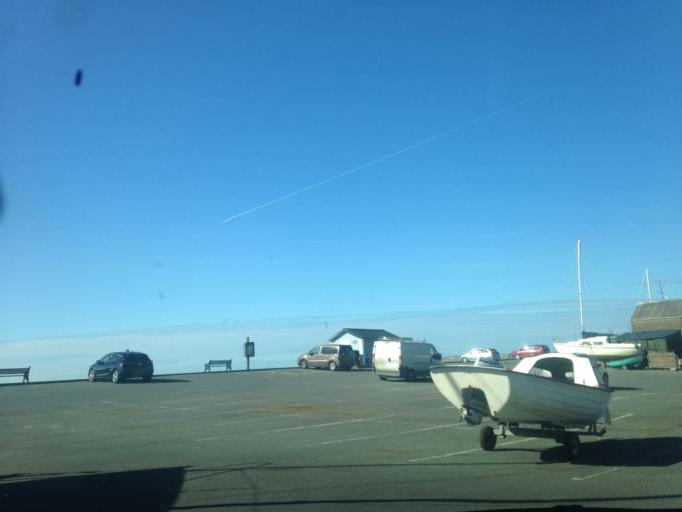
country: GB
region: Wales
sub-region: County of Ceredigion
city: Aberaeron
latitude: 52.2426
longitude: -4.2653
